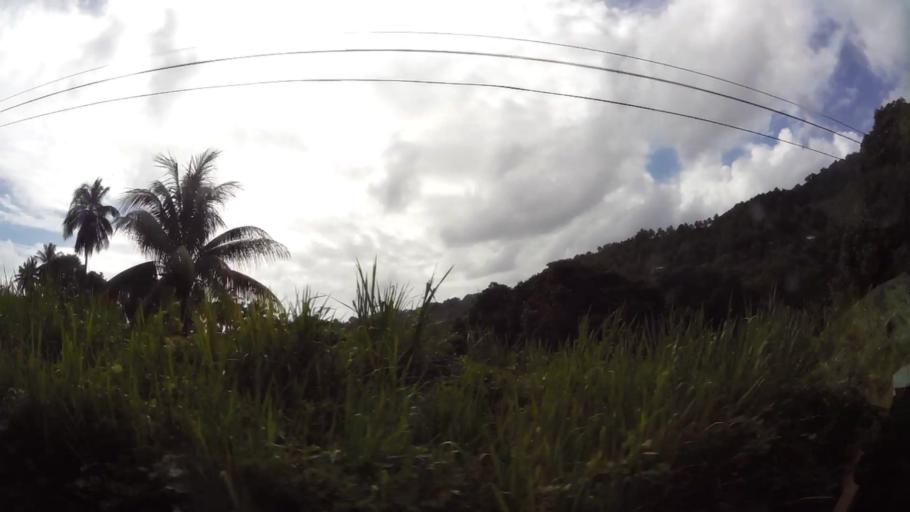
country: DM
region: Saint David
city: Castle Bruce
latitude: 15.4657
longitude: -61.2498
